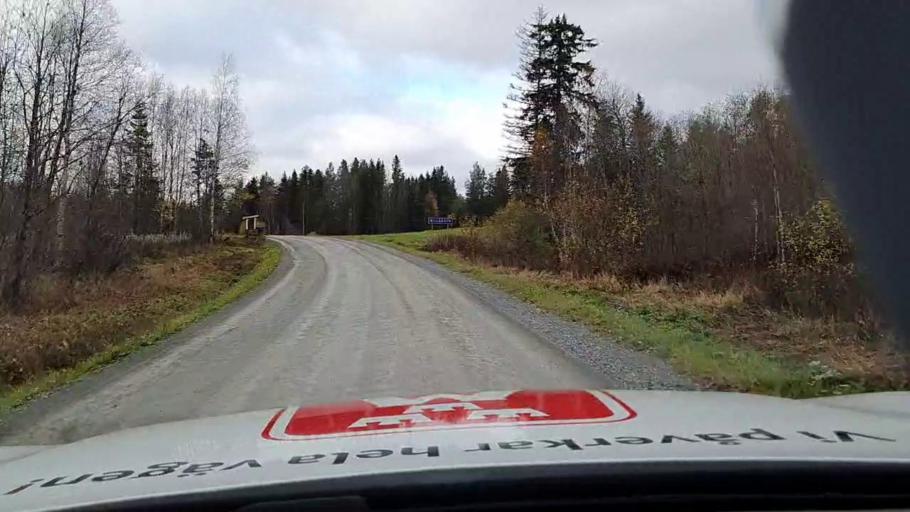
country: SE
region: Jaemtland
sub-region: Bergs Kommun
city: Hoverberg
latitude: 62.9787
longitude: 14.2152
